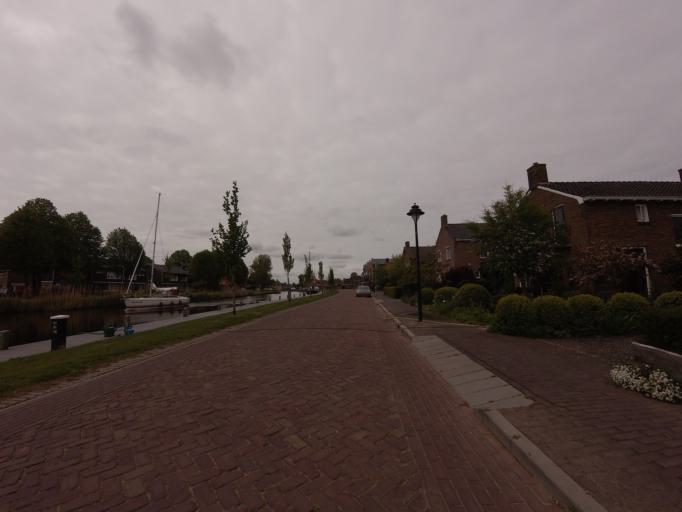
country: NL
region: Friesland
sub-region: Sudwest Fryslan
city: Workum
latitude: 52.9812
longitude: 5.4482
